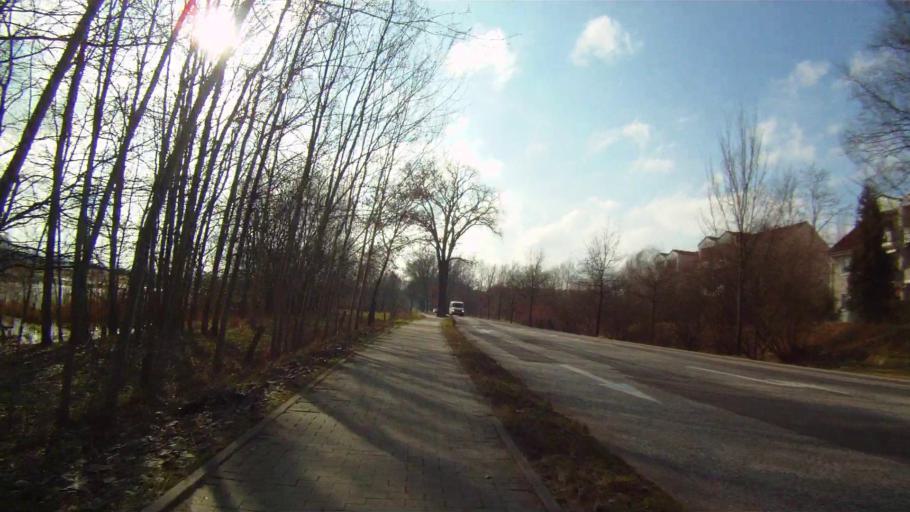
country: DE
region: Brandenburg
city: Erkner
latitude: 52.4075
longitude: 13.7500
